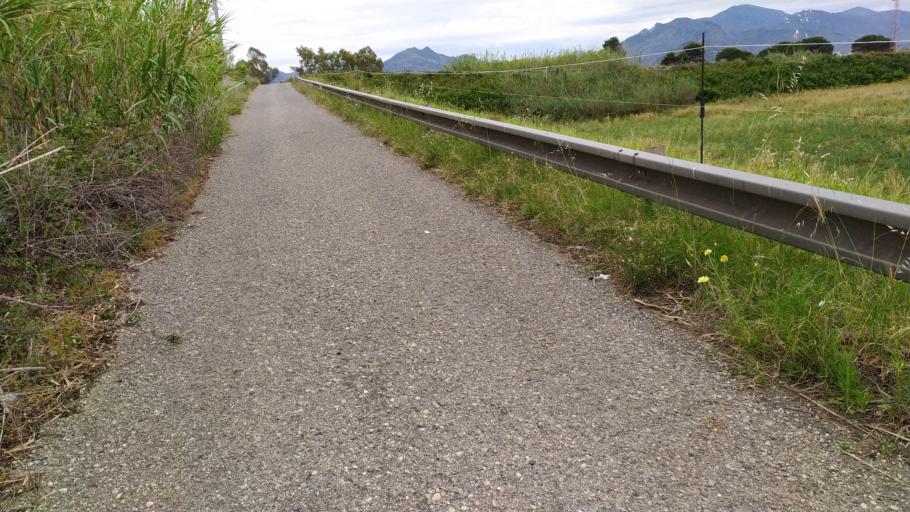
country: IT
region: Sicily
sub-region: Messina
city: San Filippo del Mela
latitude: 38.1867
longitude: 15.2594
